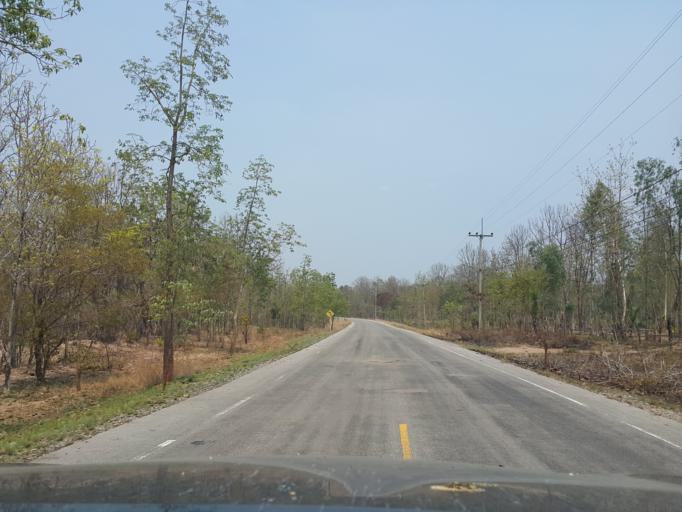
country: TH
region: Lampang
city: Mae Phrik
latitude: 17.5567
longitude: 99.1037
